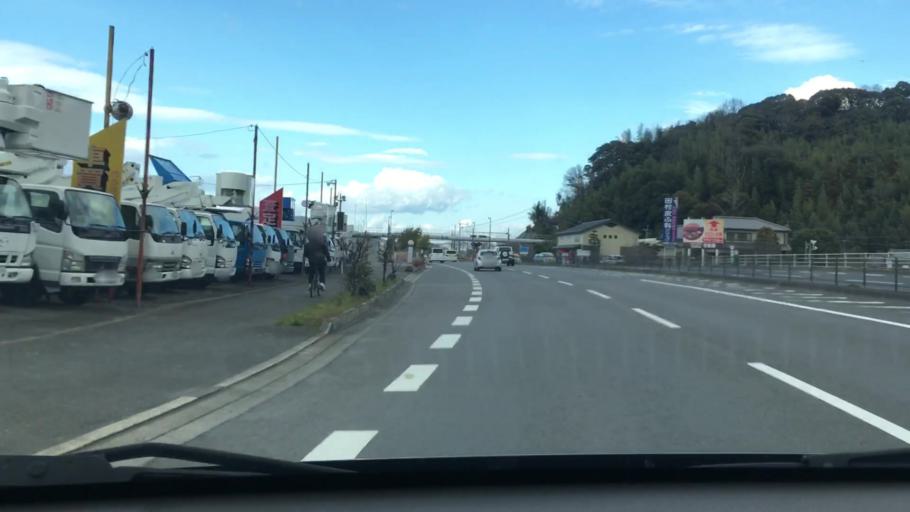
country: JP
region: Oita
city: Oita
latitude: 33.1348
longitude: 131.6600
